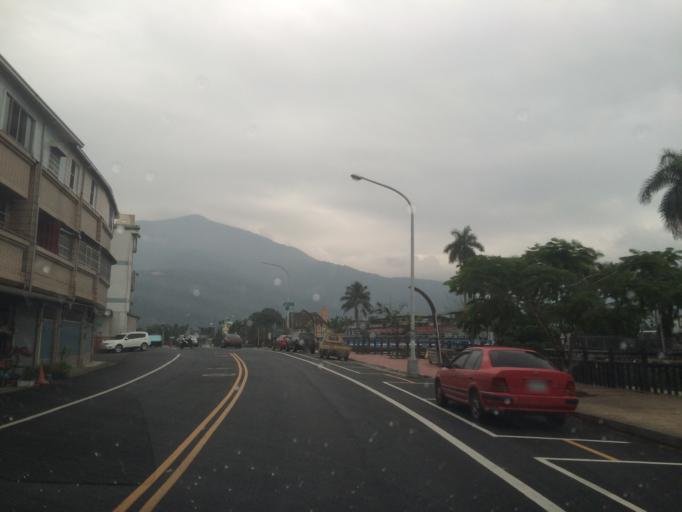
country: TW
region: Taiwan
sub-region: Nantou
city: Puli
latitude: 23.9566
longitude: 120.9696
